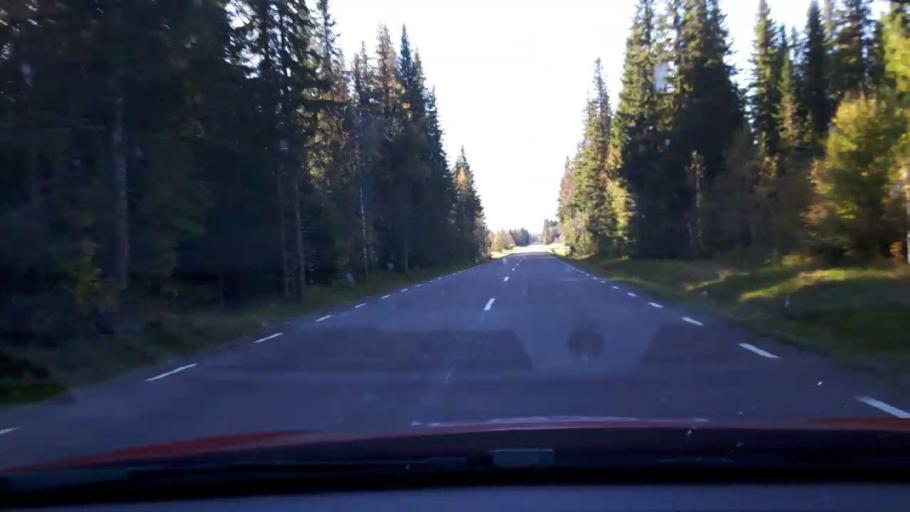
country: SE
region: Jaemtland
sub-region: Stroemsunds Kommun
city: Stroemsund
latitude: 63.8455
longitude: 15.2994
